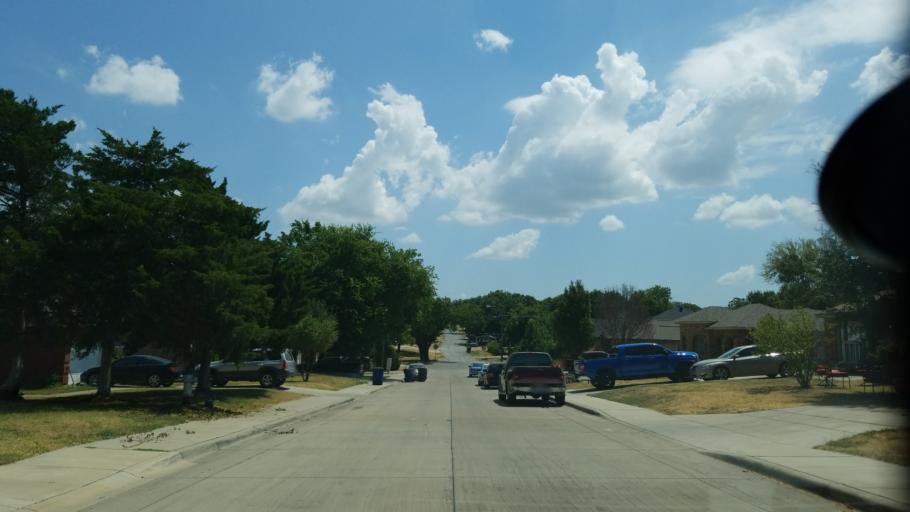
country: US
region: Texas
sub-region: Dallas County
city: Cockrell Hill
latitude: 32.7321
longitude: -96.8961
